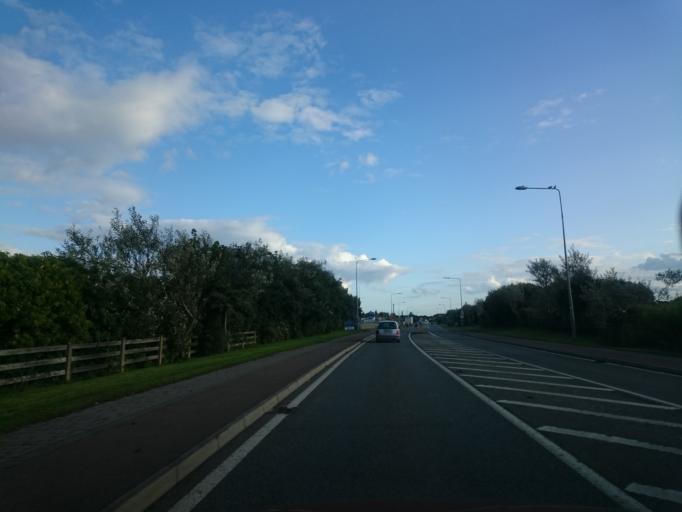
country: IE
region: Leinster
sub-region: Loch Garman
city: Ballygerry
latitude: 52.2492
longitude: -6.3441
